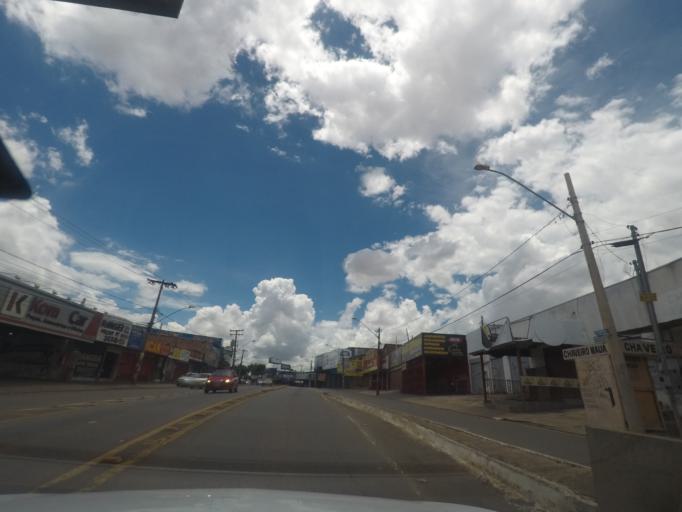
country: BR
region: Goias
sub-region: Goiania
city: Goiania
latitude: -16.6923
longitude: -49.3182
